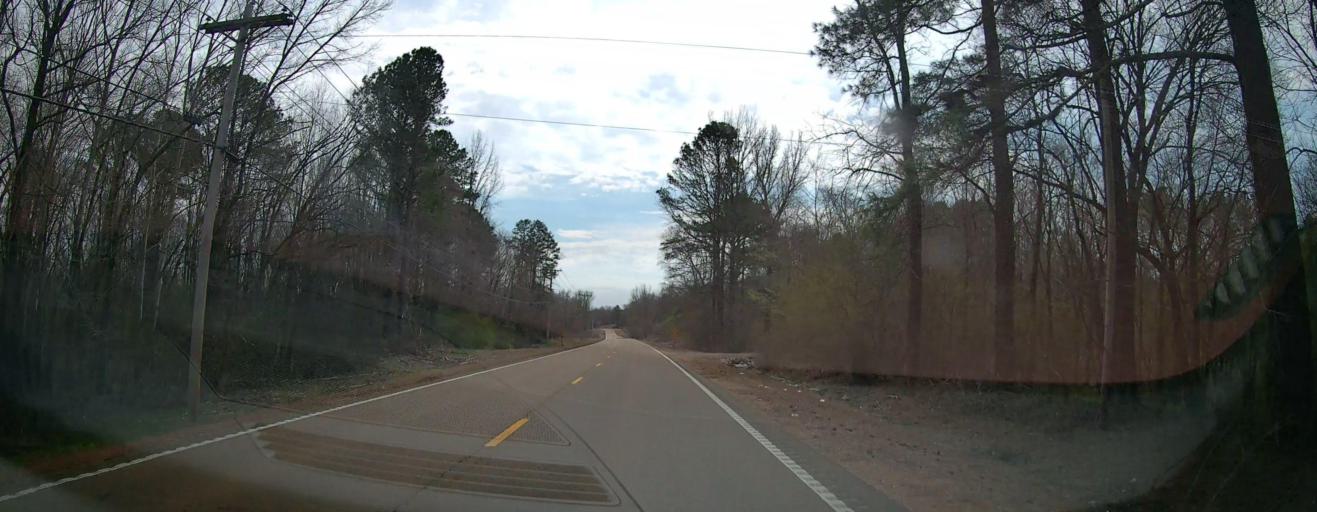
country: US
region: Mississippi
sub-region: Marshall County
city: Holly Springs
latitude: 34.7270
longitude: -89.4179
